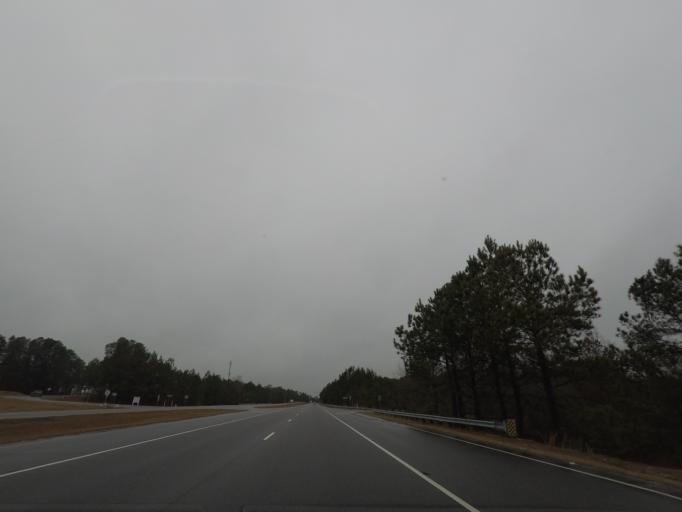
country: US
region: North Carolina
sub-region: Lee County
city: Broadway
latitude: 35.3382
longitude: -79.0983
